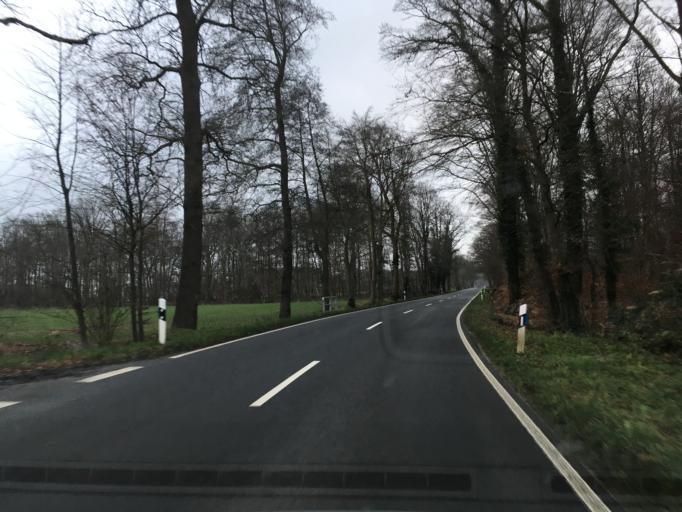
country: DE
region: North Rhine-Westphalia
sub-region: Regierungsbezirk Munster
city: Heek
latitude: 52.1685
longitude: 7.1090
